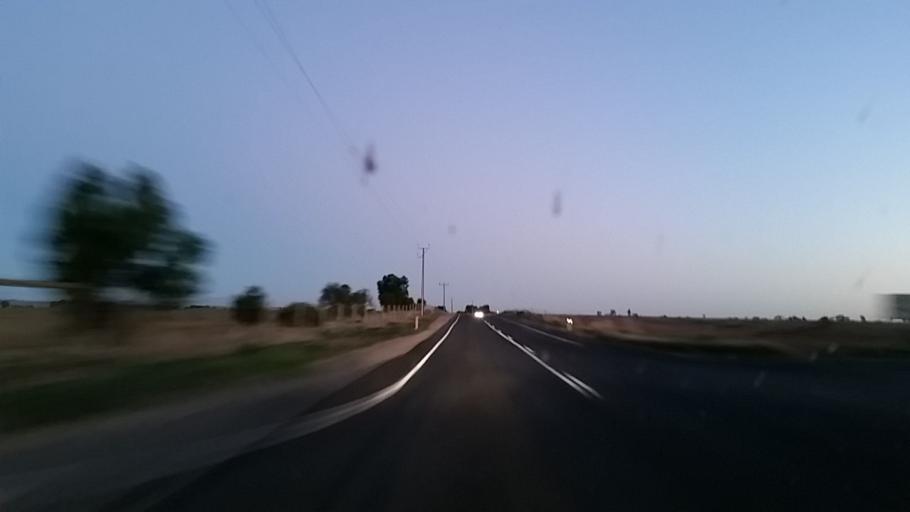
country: AU
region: South Australia
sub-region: Wakefield
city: Balaklava
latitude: -34.1763
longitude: 138.4399
